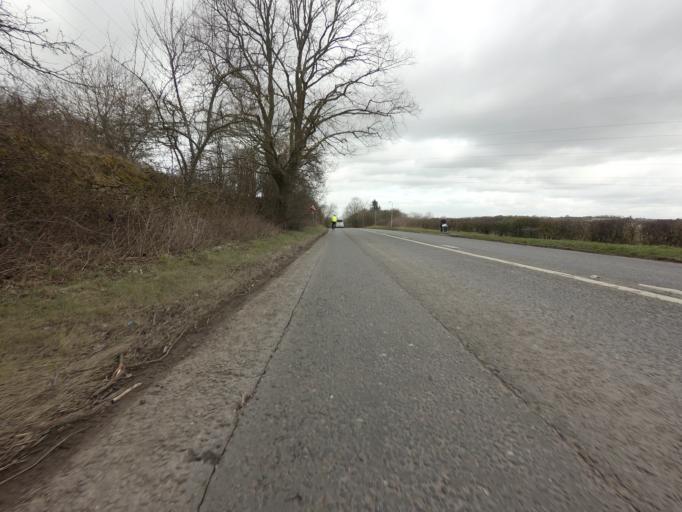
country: GB
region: England
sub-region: Lincolnshire
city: Grantham
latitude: 52.8969
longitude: -0.6343
